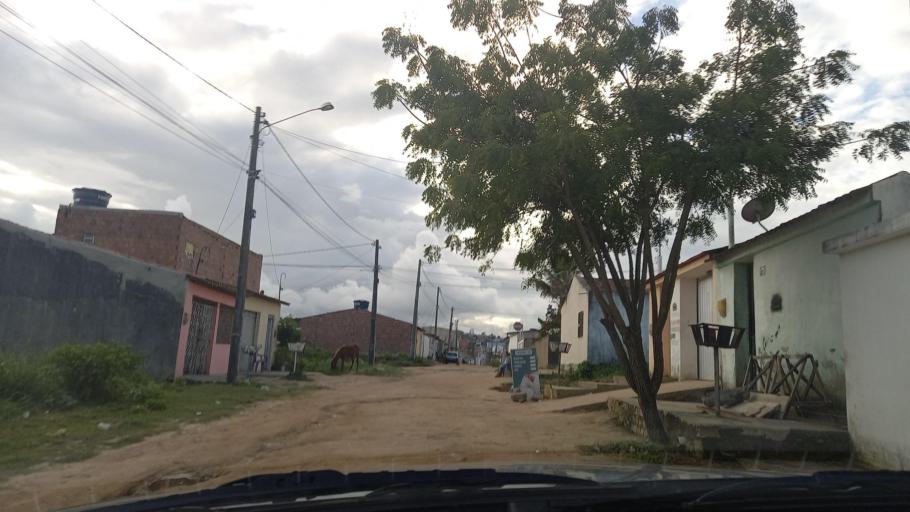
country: BR
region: Pernambuco
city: Garanhuns
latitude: -8.9154
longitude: -36.4819
